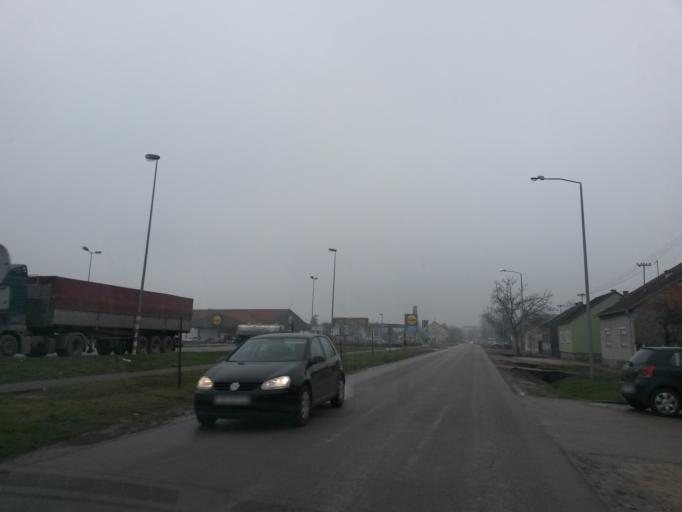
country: HR
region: Vukovarsko-Srijemska
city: Zupanja
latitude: 45.0802
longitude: 18.6973
